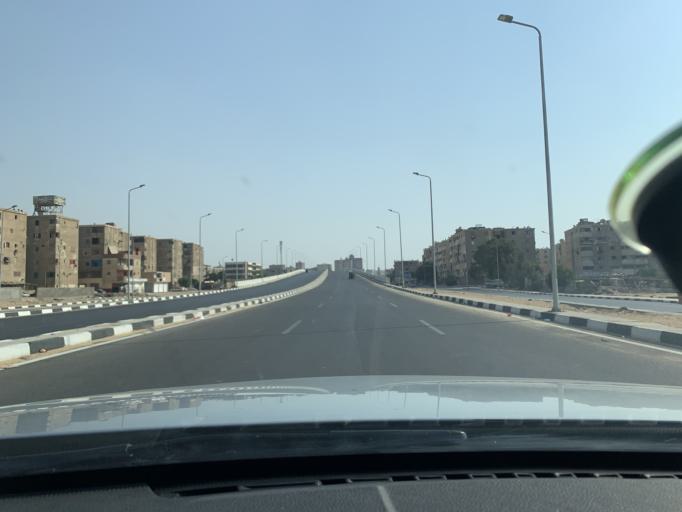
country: EG
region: Muhafazat al Qalyubiyah
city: Al Khankah
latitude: 30.1707
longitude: 31.4132
